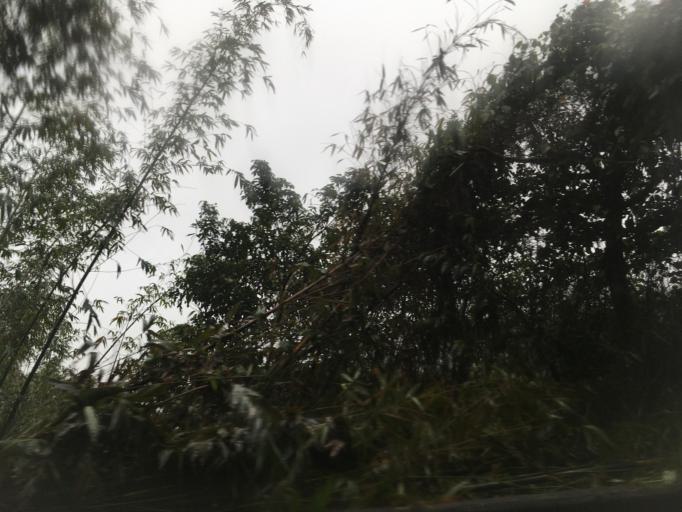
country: TW
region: Taiwan
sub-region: Keelung
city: Keelung
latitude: 25.0708
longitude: 121.9054
